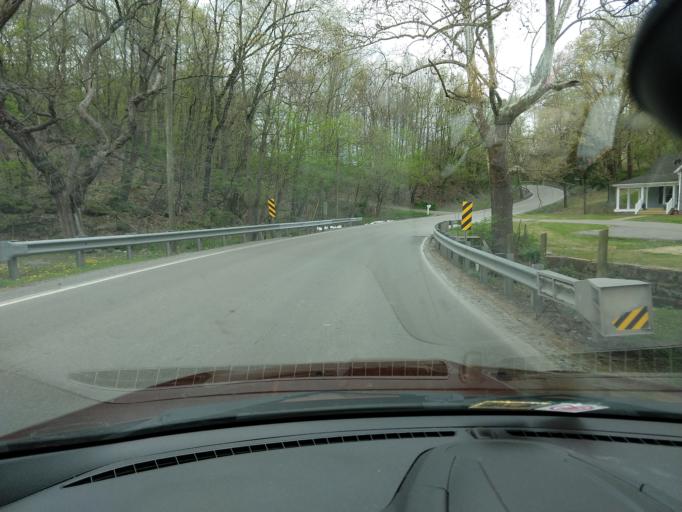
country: US
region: West Virginia
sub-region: Harrison County
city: Despard
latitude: 39.3292
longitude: -80.2890
